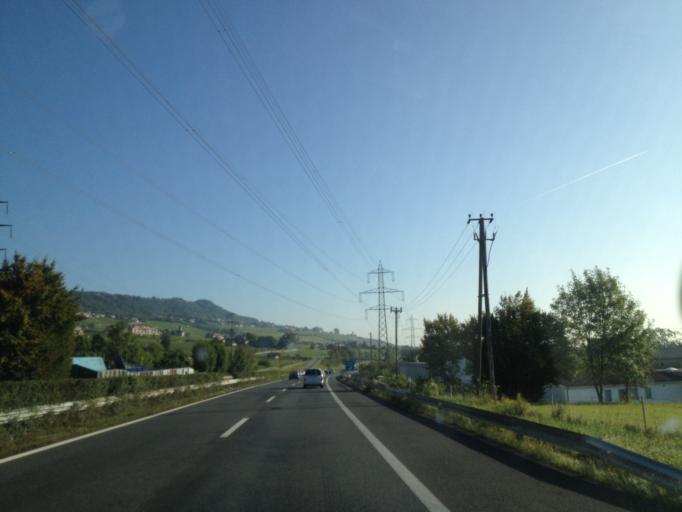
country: CH
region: Vaud
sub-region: Nyon District
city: Rolle
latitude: 46.4617
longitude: 6.3259
